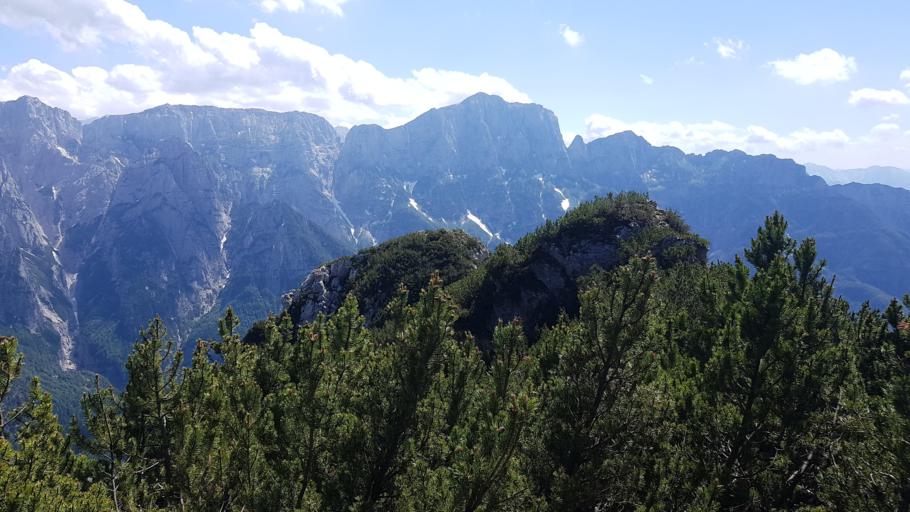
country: IT
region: Friuli Venezia Giulia
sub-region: Provincia di Udine
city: Malborghetto
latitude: 46.4728
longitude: 13.3995
